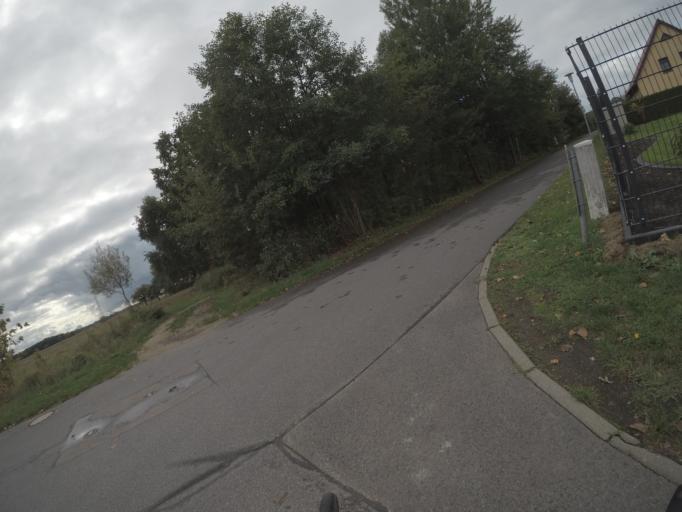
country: DE
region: Berlin
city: Buch
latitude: 52.6804
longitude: 13.4675
